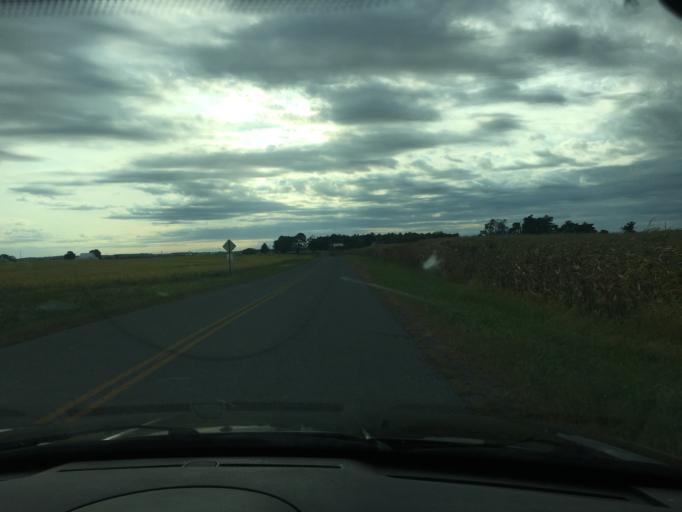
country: US
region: Ohio
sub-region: Logan County
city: West Liberty
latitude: 40.2716
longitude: -83.7161
